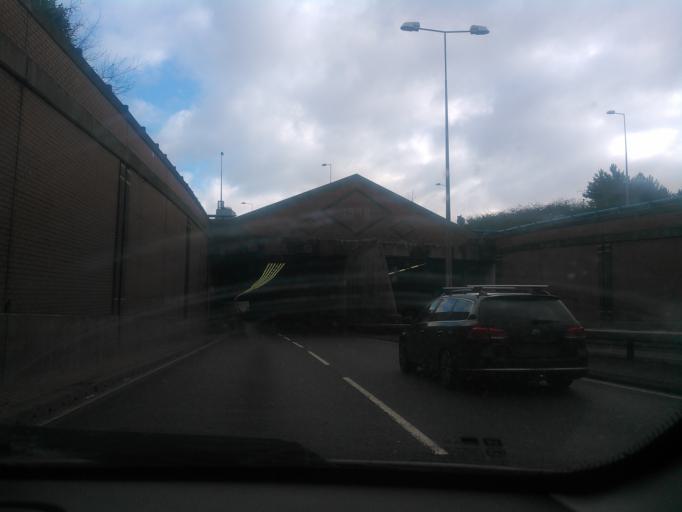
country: GB
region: England
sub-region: Staffordshire
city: Longton
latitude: 52.9785
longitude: -2.1065
